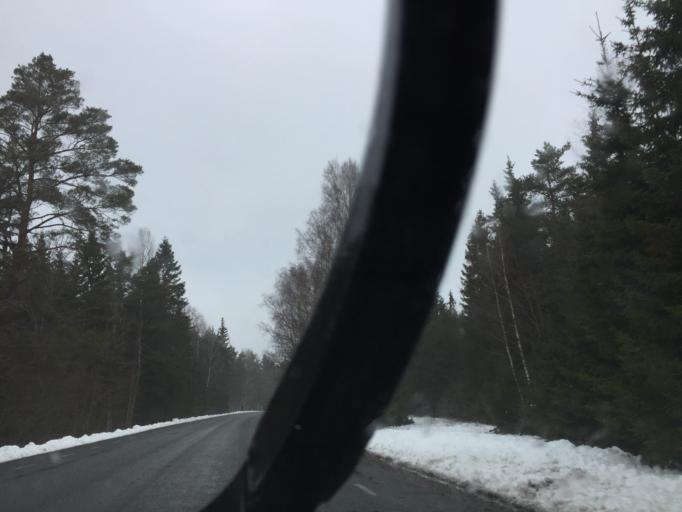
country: EE
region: Saare
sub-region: Kuressaare linn
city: Kuressaare
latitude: 58.2935
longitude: 22.0244
